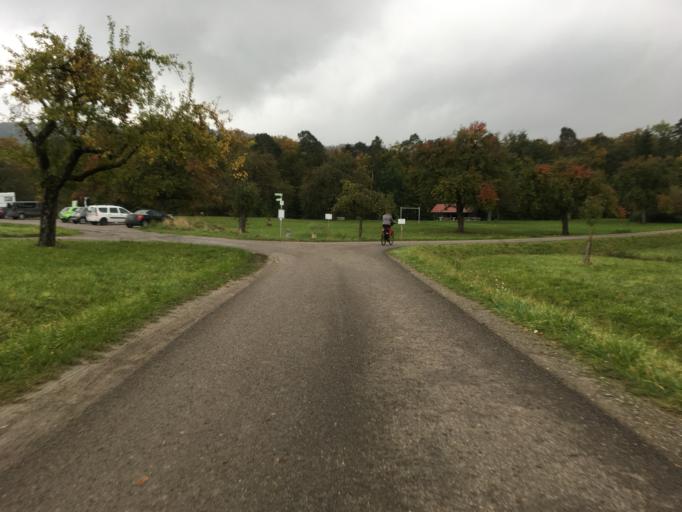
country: DE
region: Baden-Wuerttemberg
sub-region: Tuebingen Region
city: Nehren
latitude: 48.4250
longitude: 9.0803
